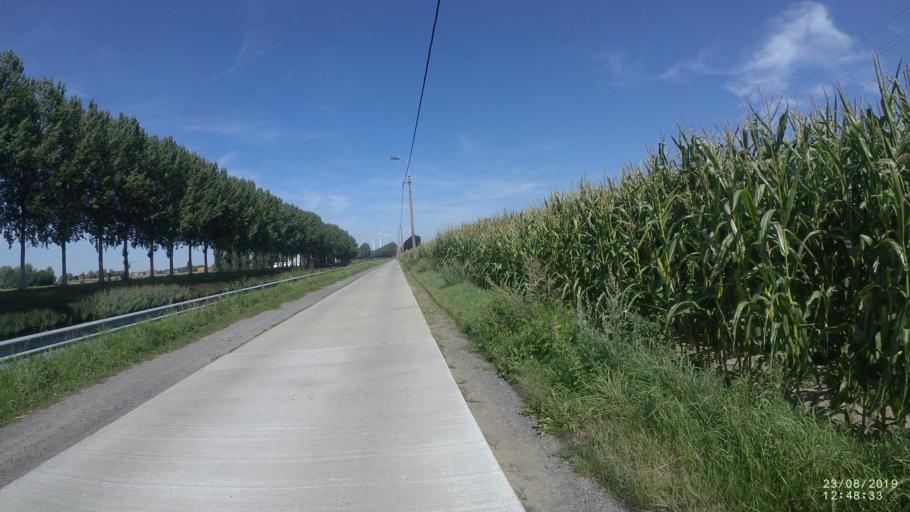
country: BE
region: Flanders
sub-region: Provincie Oost-Vlaanderen
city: Eeklo
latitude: 51.1663
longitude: 3.5429
